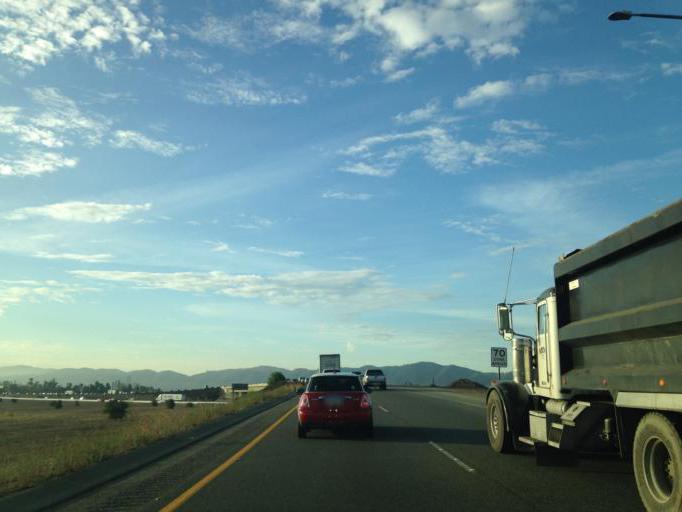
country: US
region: California
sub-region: Riverside County
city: Murrieta Hot Springs
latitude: 33.5517
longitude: -117.1815
